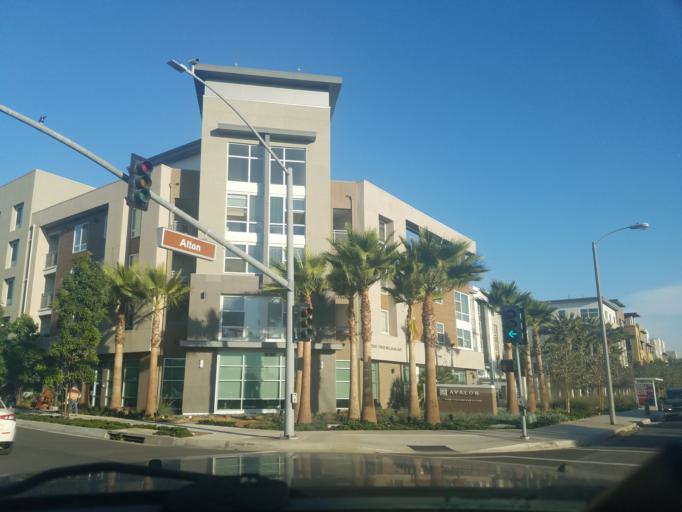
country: US
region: California
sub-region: Orange County
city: Irvine
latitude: 33.6903
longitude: -117.8345
